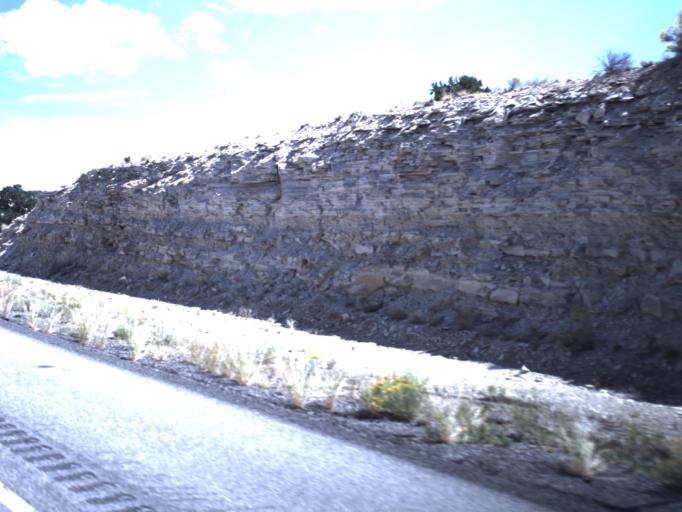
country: US
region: Utah
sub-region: Emery County
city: Ferron
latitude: 38.8556
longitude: -110.9139
